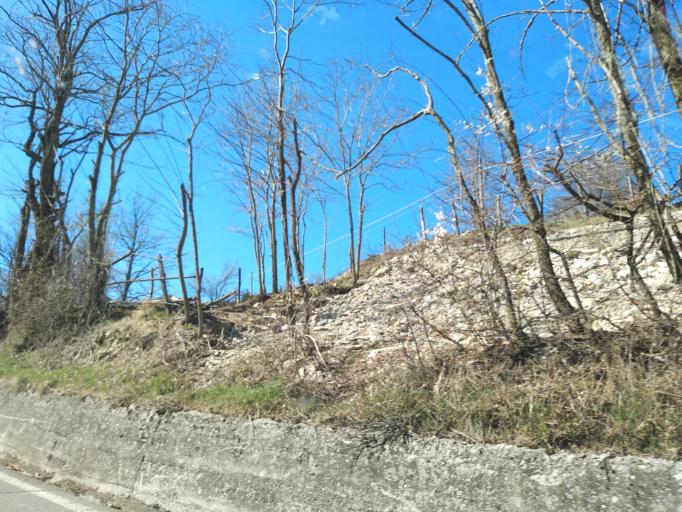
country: IT
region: Emilia-Romagna
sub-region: Provincia di Reggio Emilia
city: Ramiseto
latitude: 44.4066
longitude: 10.2716
